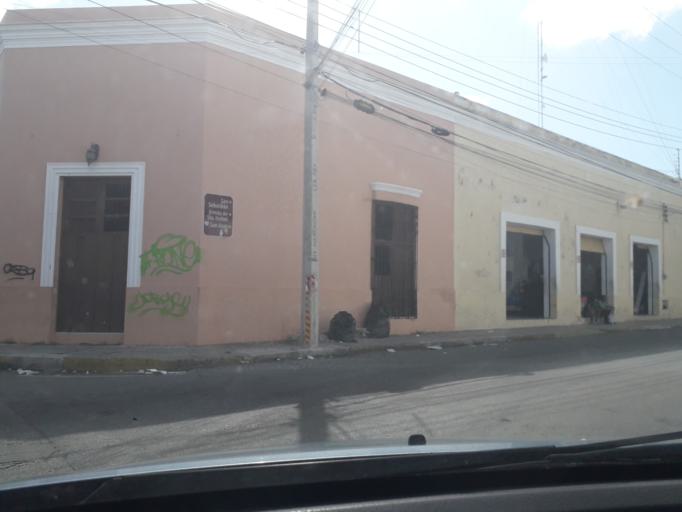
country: MX
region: Yucatan
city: Merida
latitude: 20.9597
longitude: -89.6233
